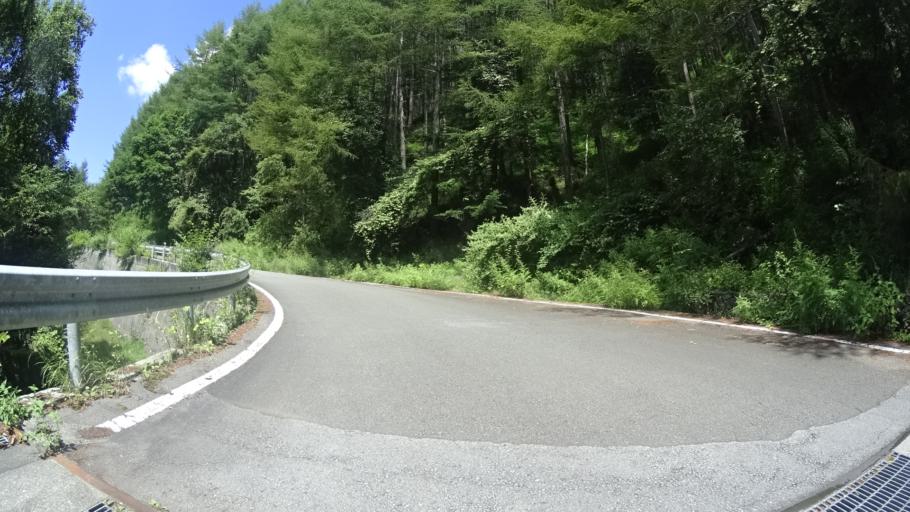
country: JP
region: Yamanashi
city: Enzan
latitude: 35.8403
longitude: 138.6436
